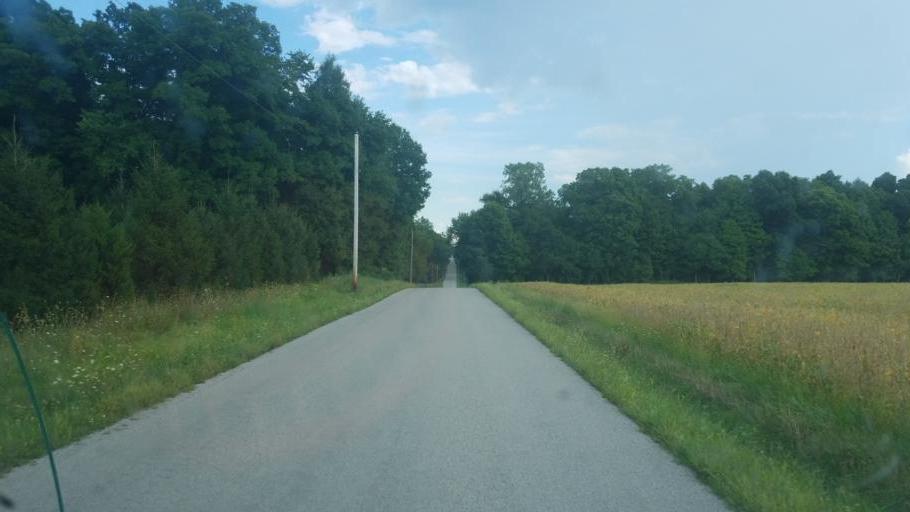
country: US
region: Ohio
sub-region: Huron County
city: Plymouth
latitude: 41.0212
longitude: -82.6704
